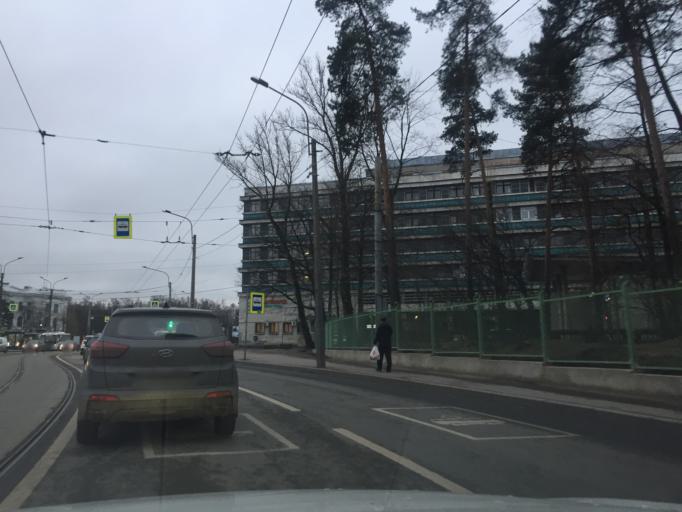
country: RU
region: St.-Petersburg
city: Kushelevka
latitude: 60.0094
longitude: 30.3690
